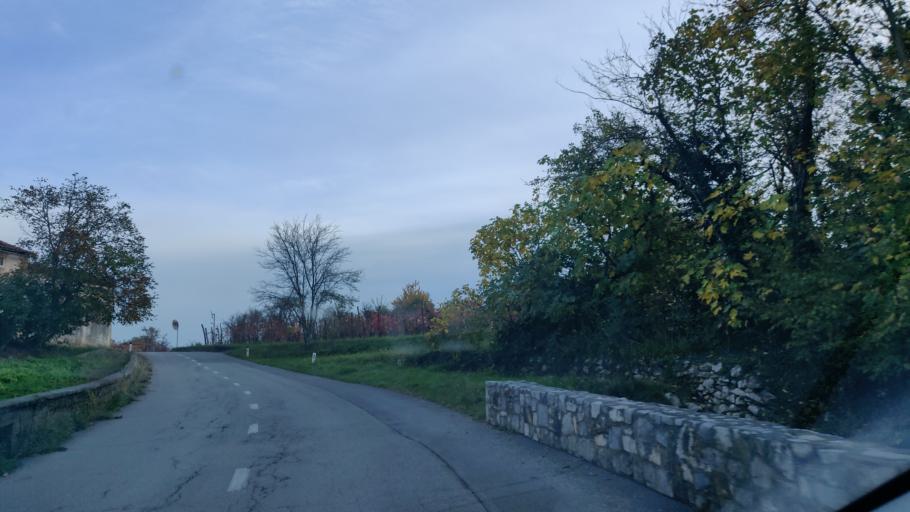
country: SI
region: Sezana
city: Sezana
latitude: 45.7882
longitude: 13.8618
